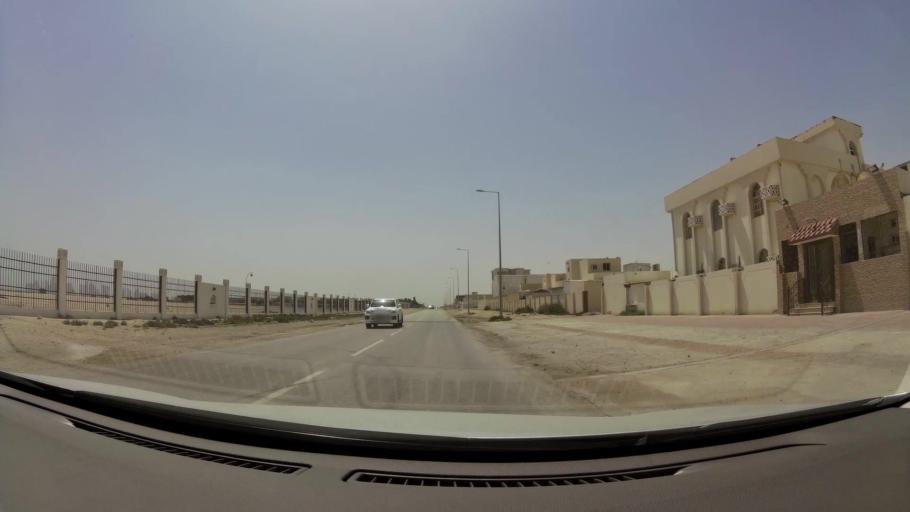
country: QA
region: Baladiyat Umm Salal
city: Umm Salal Muhammad
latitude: 25.3670
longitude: 51.4790
